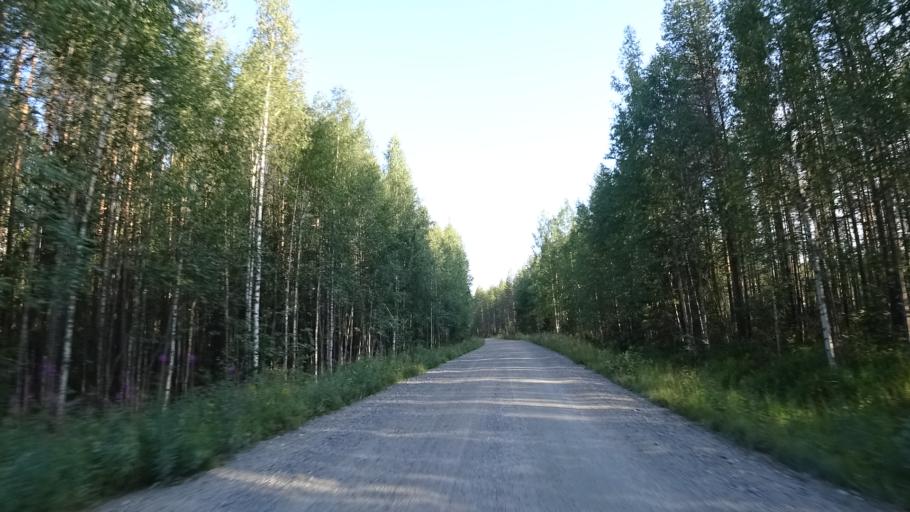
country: FI
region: North Karelia
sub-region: Joensuu
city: Ilomantsi
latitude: 63.1348
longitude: 30.7073
